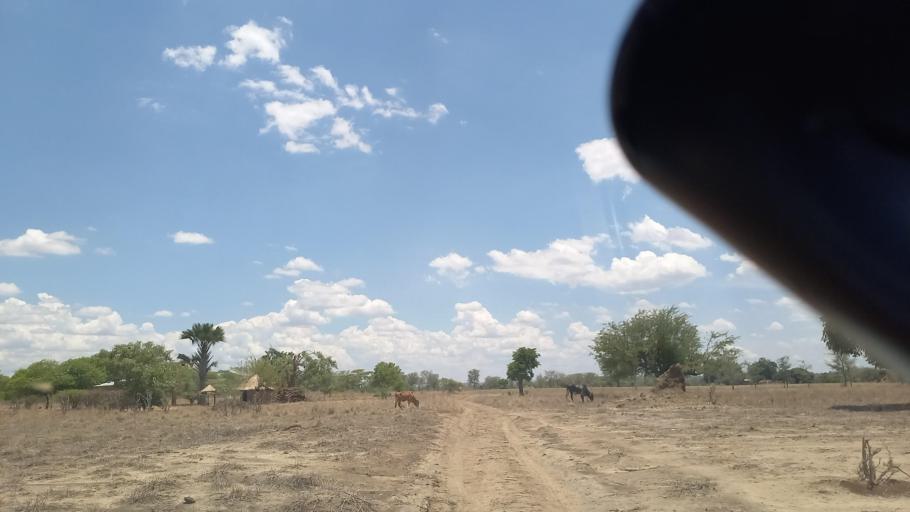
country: ZM
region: Southern
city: Mazabuka
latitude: -16.1271
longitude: 27.7790
